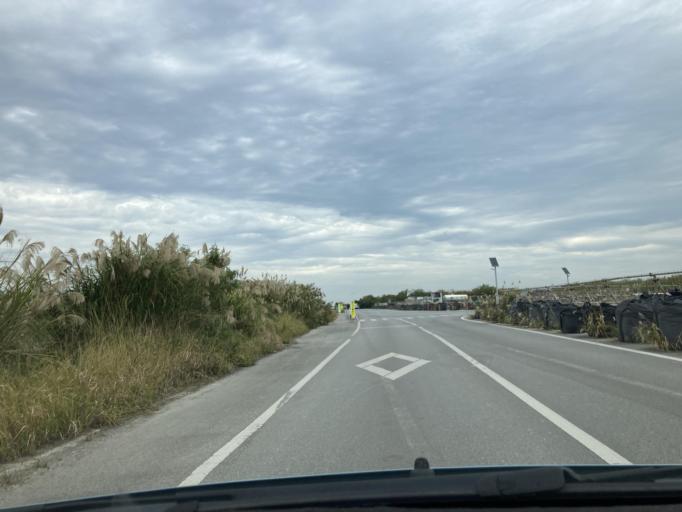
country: JP
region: Okinawa
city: Okinawa
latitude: 26.3864
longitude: 127.7459
